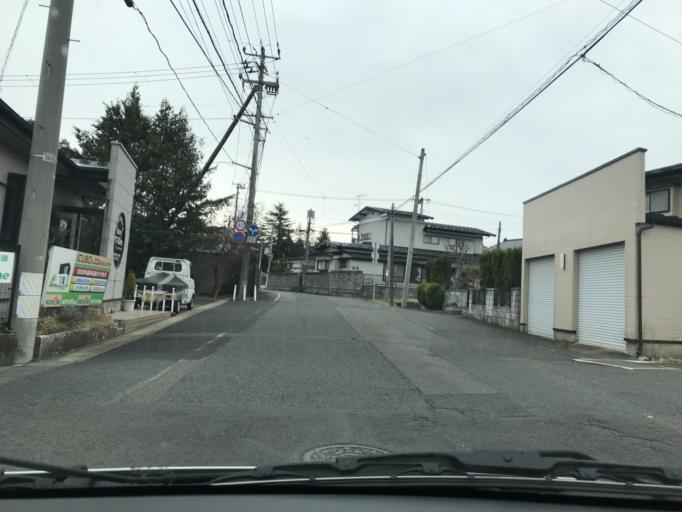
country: JP
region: Iwate
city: Mizusawa
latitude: 39.1366
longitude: 141.1324
